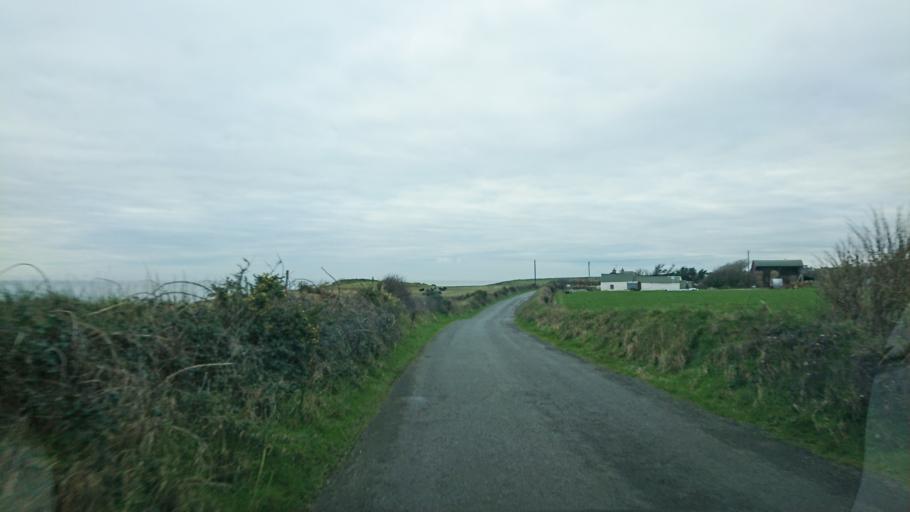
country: IE
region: Munster
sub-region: Waterford
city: Tra Mhor
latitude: 52.1394
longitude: -7.1761
